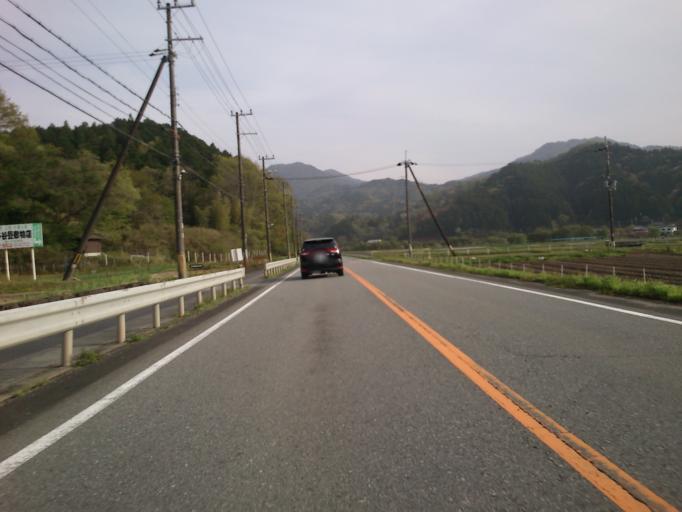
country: JP
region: Hyogo
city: Sasayama
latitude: 35.0866
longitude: 135.3186
